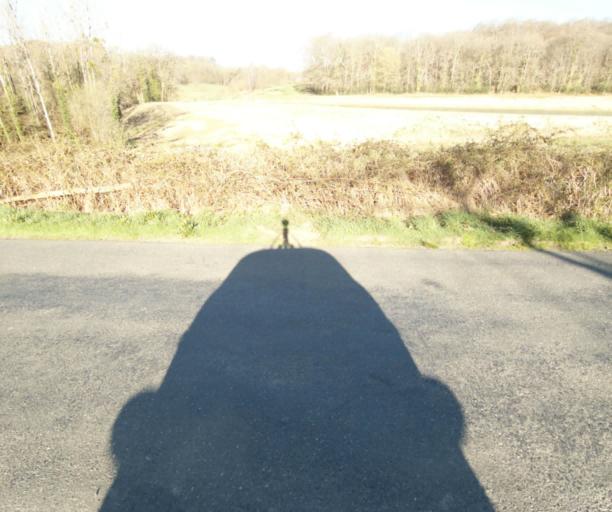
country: FR
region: Limousin
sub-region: Departement de la Correze
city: Uzerche
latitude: 45.3808
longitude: 1.6112
